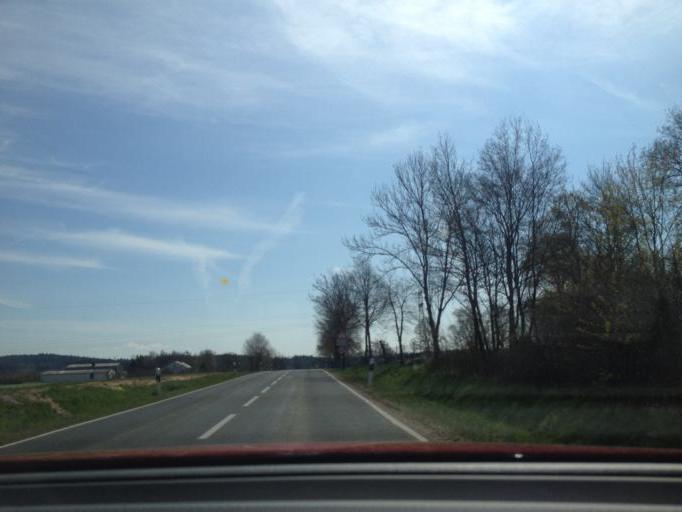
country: DE
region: Bavaria
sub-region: Upper Franconia
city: Roslau
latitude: 50.0790
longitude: 12.0070
